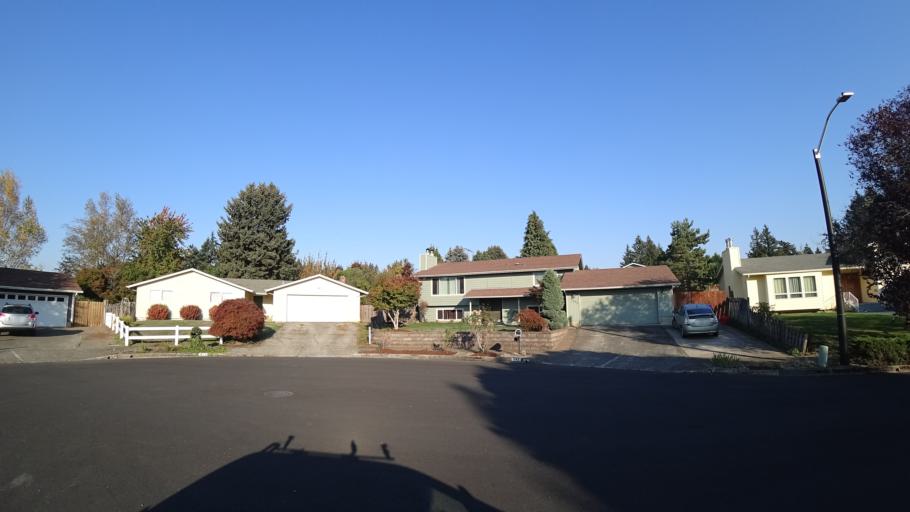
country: US
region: Oregon
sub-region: Multnomah County
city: Gresham
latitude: 45.5078
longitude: -122.4512
